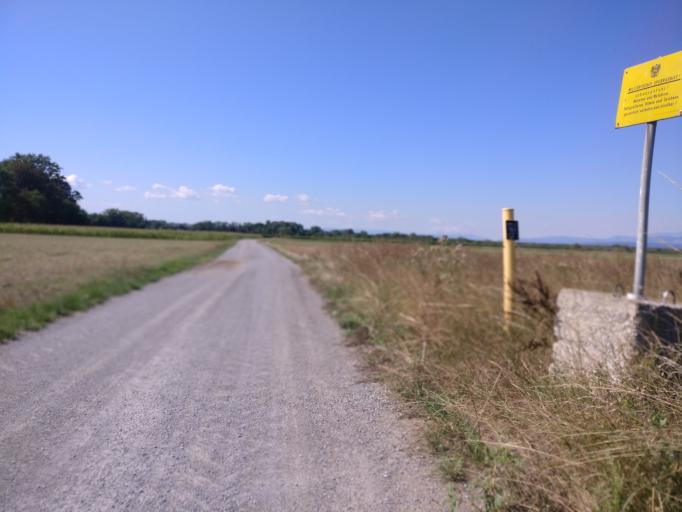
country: AT
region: Lower Austria
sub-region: Politischer Bezirk Baden
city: Pottendorf
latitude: 47.9133
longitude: 16.3546
